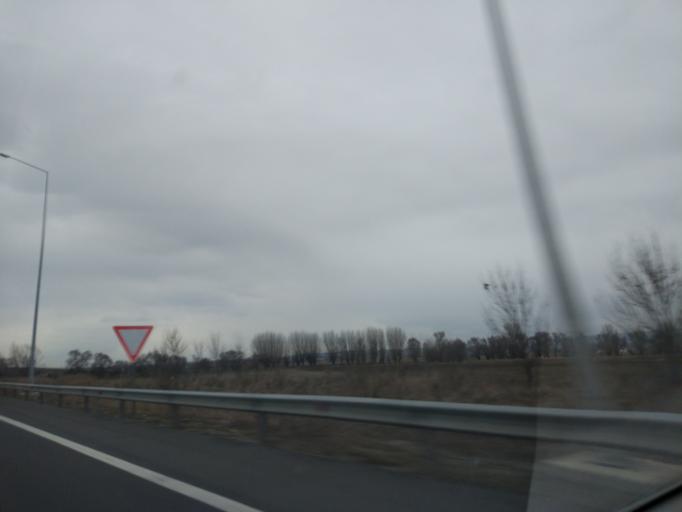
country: TR
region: Bolu
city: Gerede
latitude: 40.7395
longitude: 32.1860
